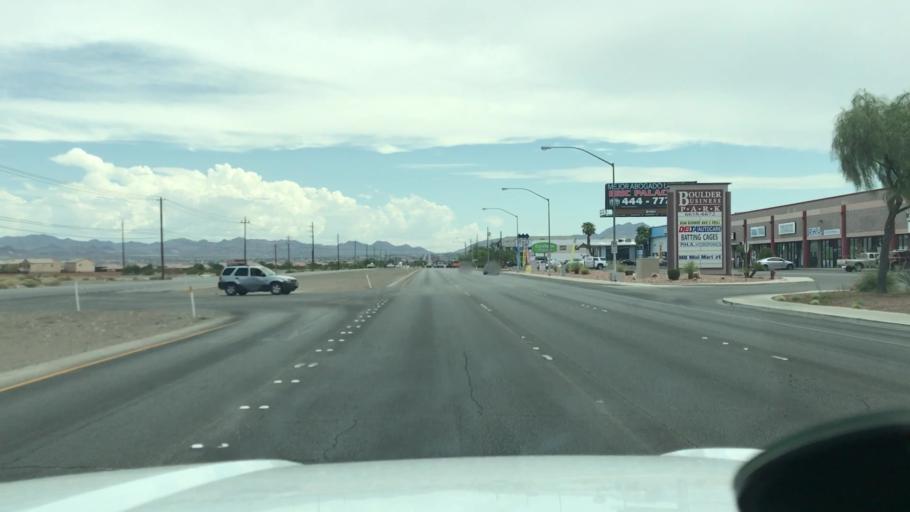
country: US
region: Nevada
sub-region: Clark County
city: Whitney
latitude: 36.0798
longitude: -115.0274
